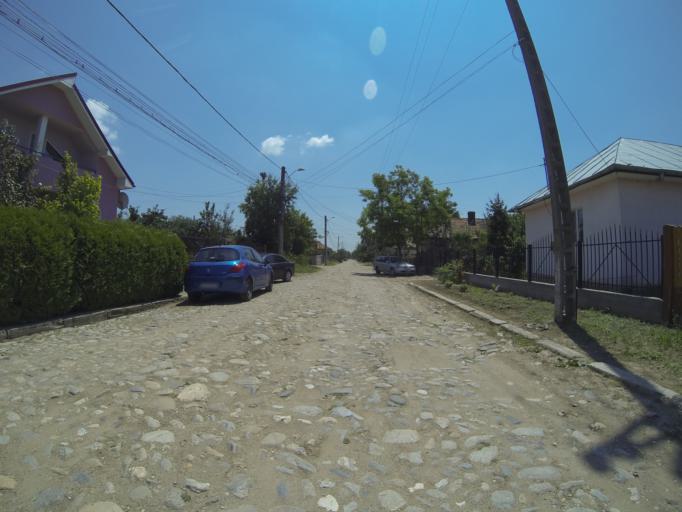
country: RO
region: Dolj
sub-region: Comuna Segarcea
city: Segarcea
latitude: 44.0914
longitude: 23.7452
